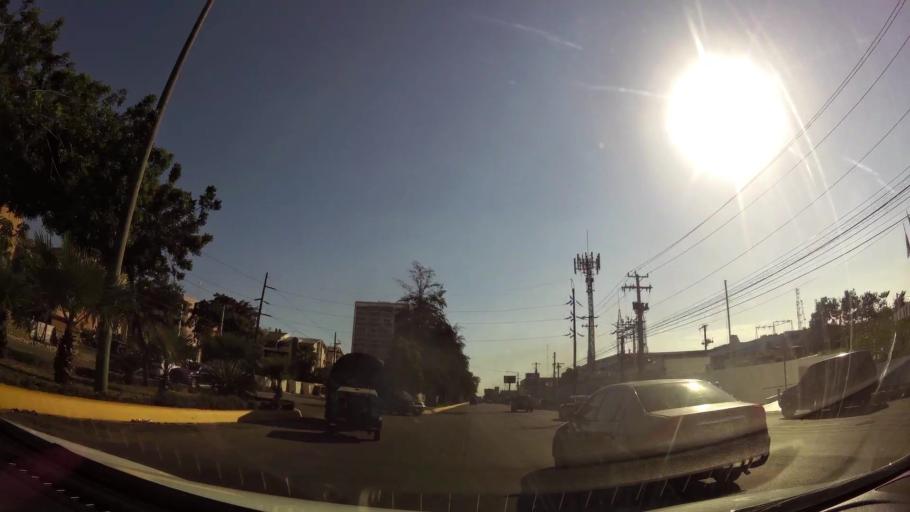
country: DO
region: Nacional
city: Bella Vista
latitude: 18.4411
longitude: -69.9786
